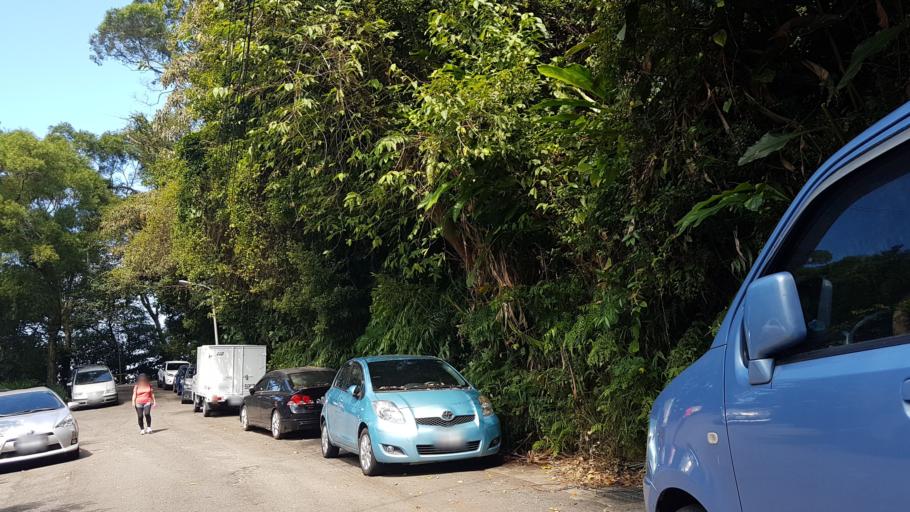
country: TW
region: Taipei
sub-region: Taipei
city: Banqiao
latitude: 24.9482
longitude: 121.5316
